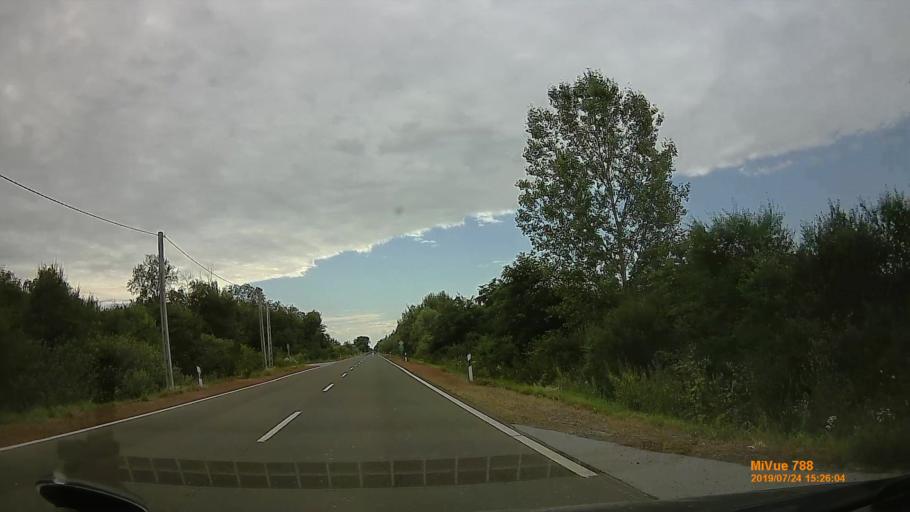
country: HU
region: Szabolcs-Szatmar-Bereg
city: Tarpa
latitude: 48.1598
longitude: 22.5311
